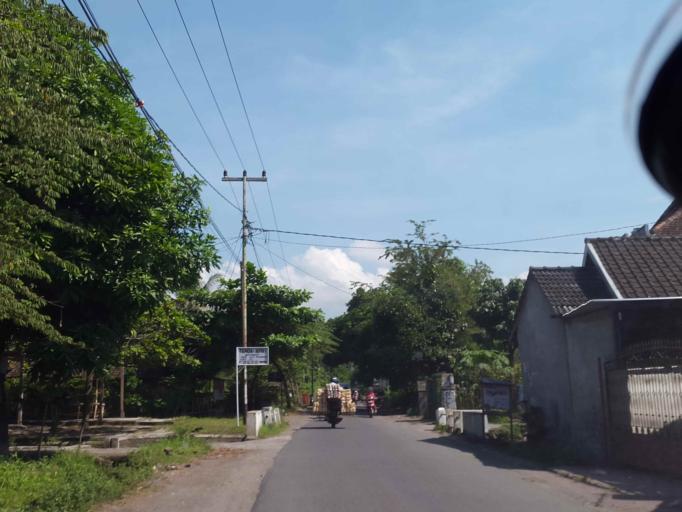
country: ID
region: West Nusa Tenggara
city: Kekeri
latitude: -8.5623
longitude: 116.1320
